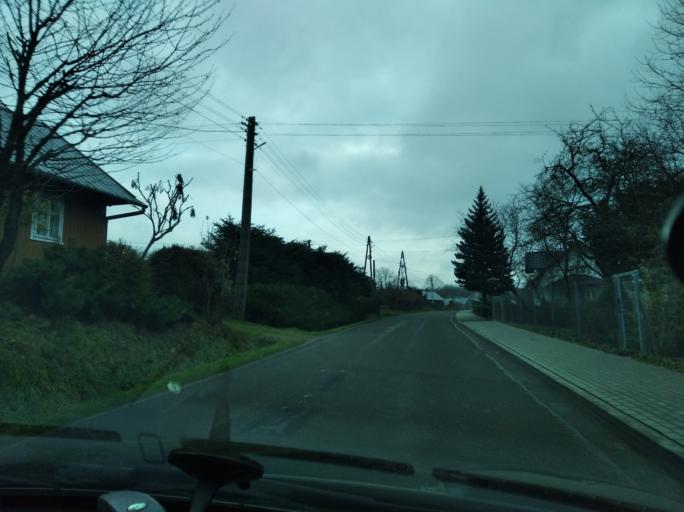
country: PL
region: Subcarpathian Voivodeship
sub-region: Powiat przeworski
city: Sietesz
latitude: 49.9978
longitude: 22.3557
